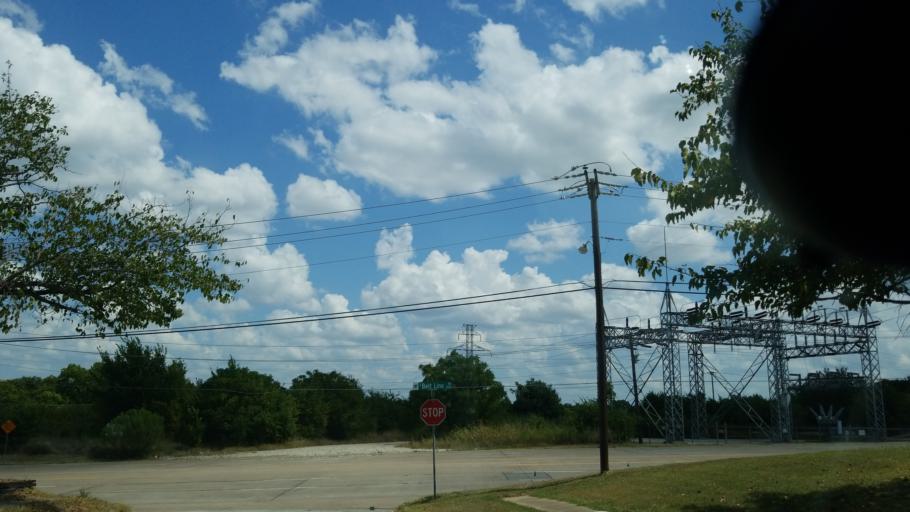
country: US
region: Texas
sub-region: Dallas County
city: Grand Prairie
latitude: 32.7300
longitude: -96.9947
